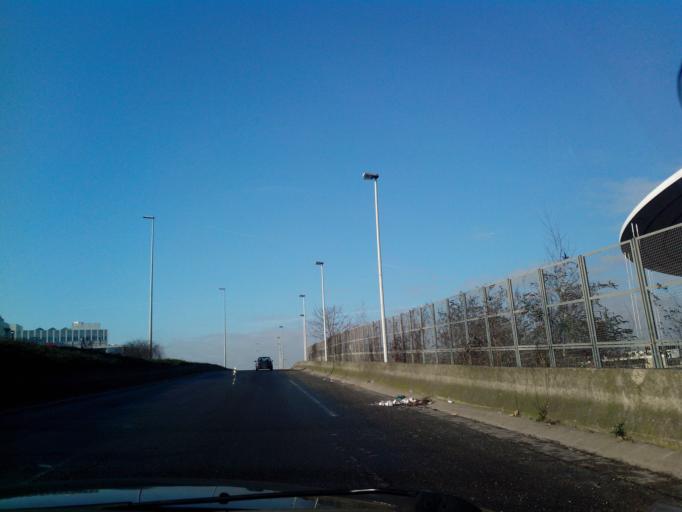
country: FR
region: Ile-de-France
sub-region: Departement de Seine-Saint-Denis
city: Saint-Denis
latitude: 48.9224
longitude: 2.3603
